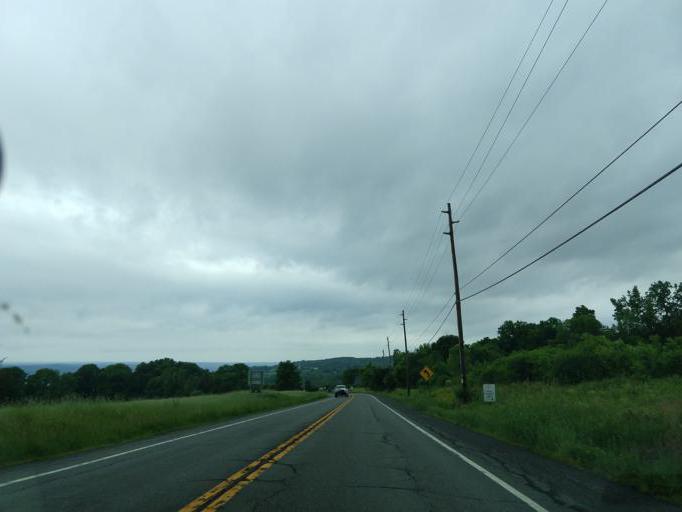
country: US
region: New York
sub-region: Tompkins County
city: Lansing
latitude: 42.5426
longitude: -76.5224
